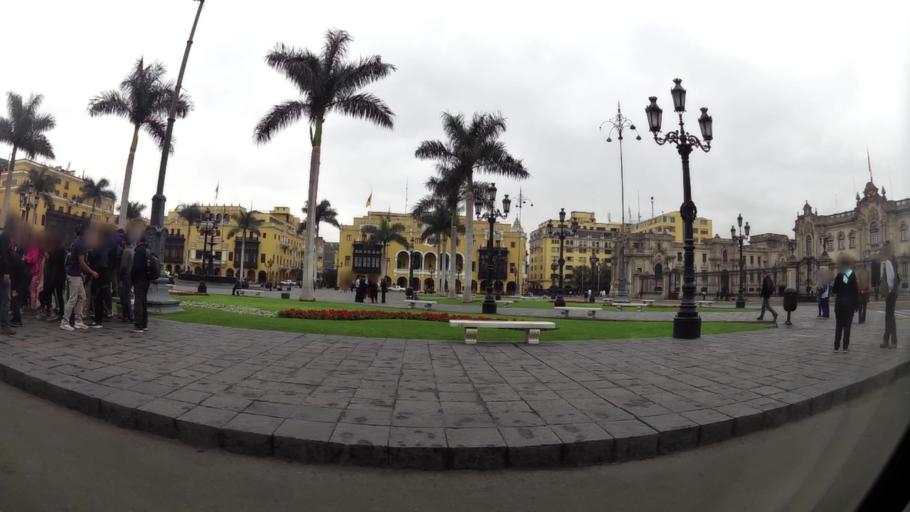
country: PE
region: Lima
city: Lima
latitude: -12.0460
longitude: -77.0300
